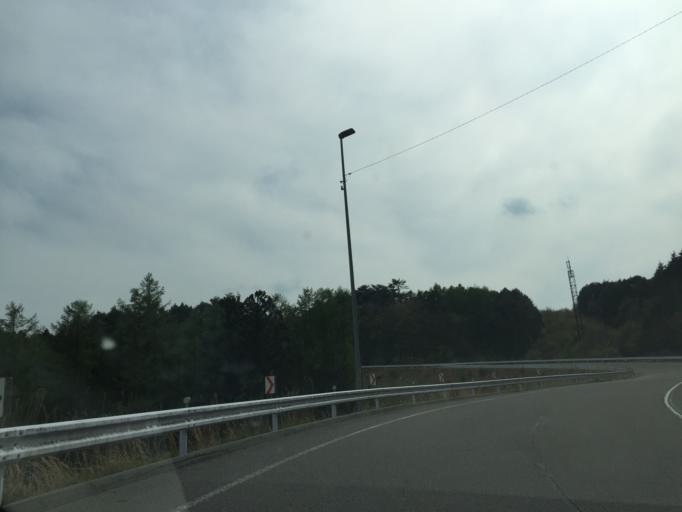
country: JP
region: Nagano
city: Iida
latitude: 35.2288
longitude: 137.7141
